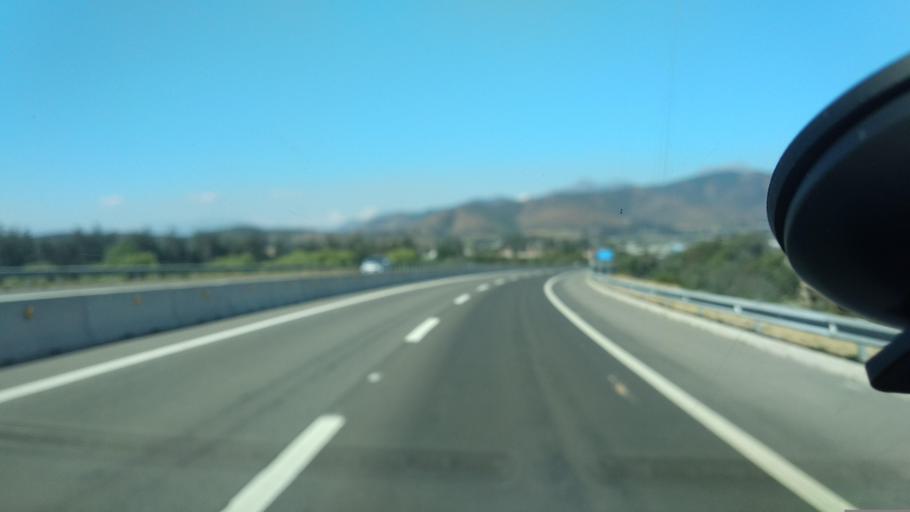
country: CL
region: Valparaiso
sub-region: Provincia de Marga Marga
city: Limache
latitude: -32.9826
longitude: -71.3162
